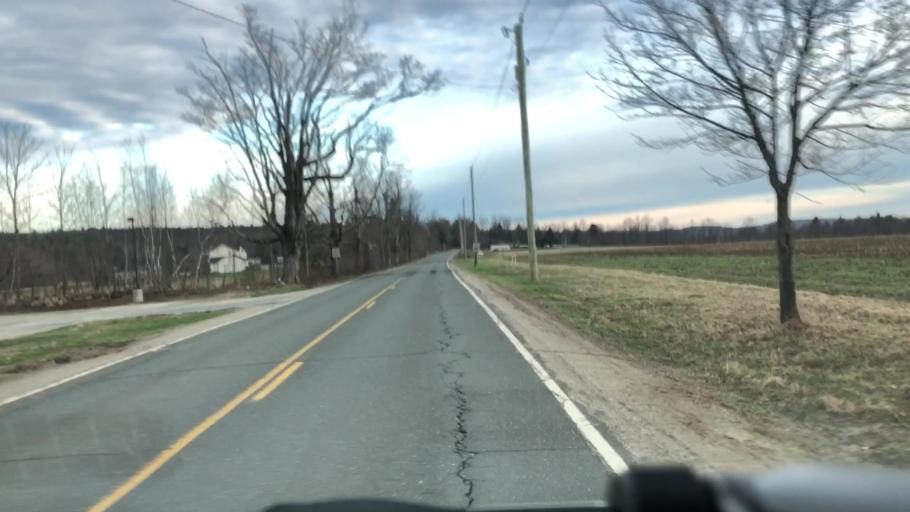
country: US
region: Massachusetts
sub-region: Hampshire County
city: Chesterfield
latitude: 42.4143
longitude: -72.9376
